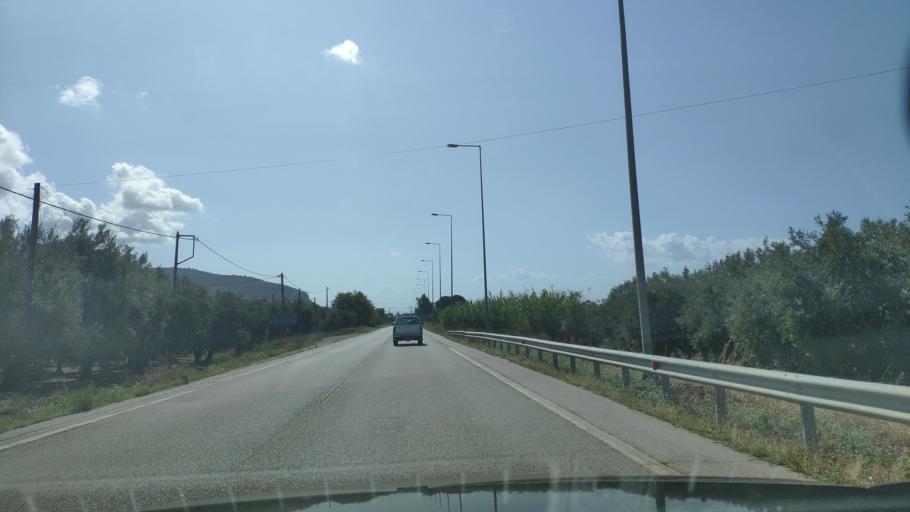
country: GR
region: West Greece
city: Aitoliko
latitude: 38.4806
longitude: 21.3532
